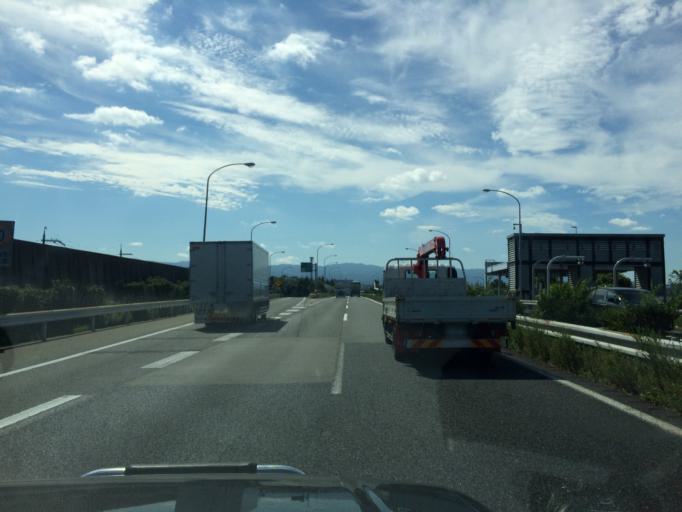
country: JP
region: Osaka
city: Takaishi
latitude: 34.5137
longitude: 135.4900
